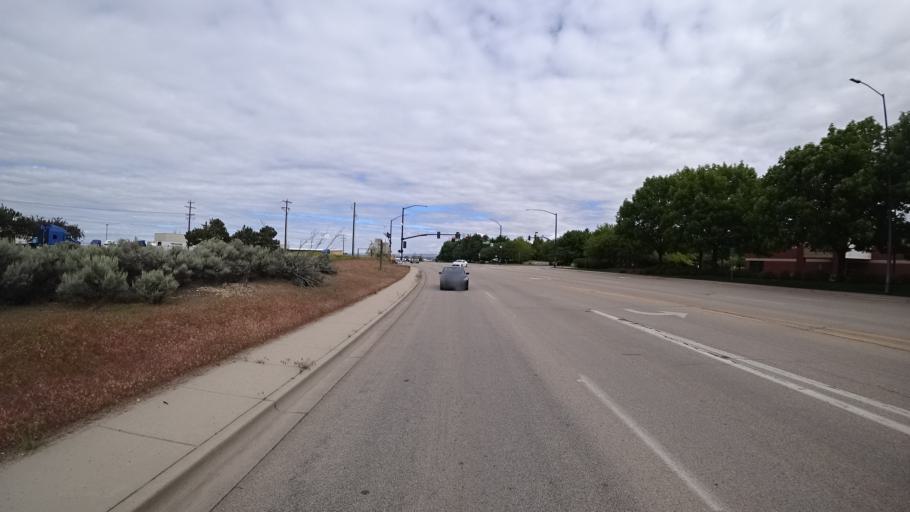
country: US
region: Idaho
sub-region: Ada County
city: Boise
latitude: 43.5428
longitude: -116.1559
